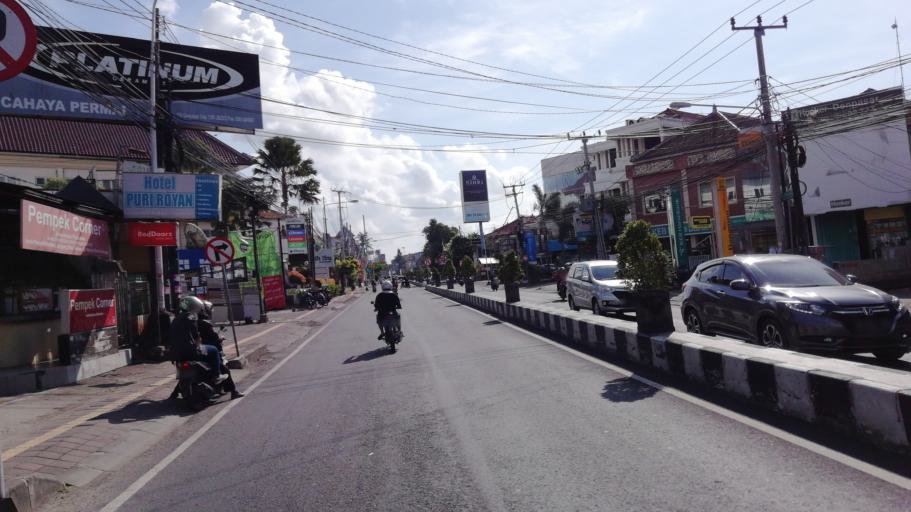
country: ID
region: Bali
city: Karyadharma
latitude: -8.6783
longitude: 115.2053
